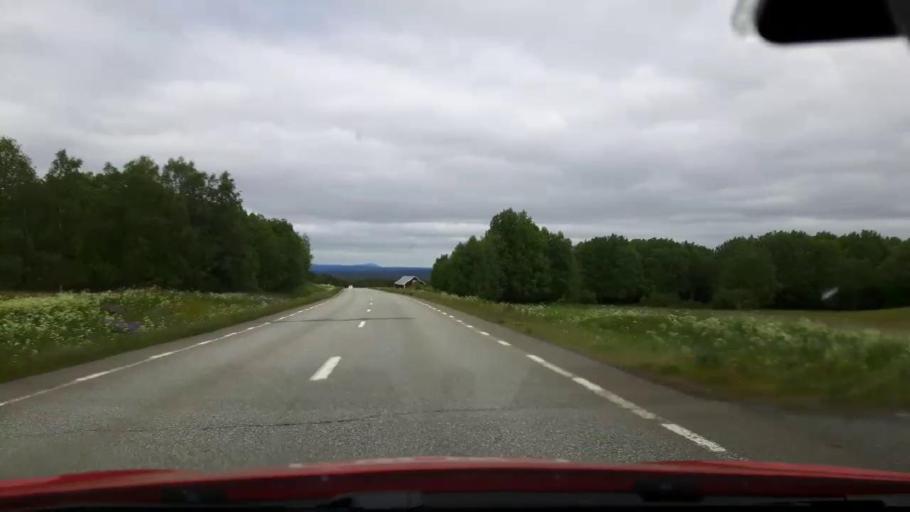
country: SE
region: Jaemtland
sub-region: Krokoms Kommun
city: Krokom
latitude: 63.5778
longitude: 14.6328
